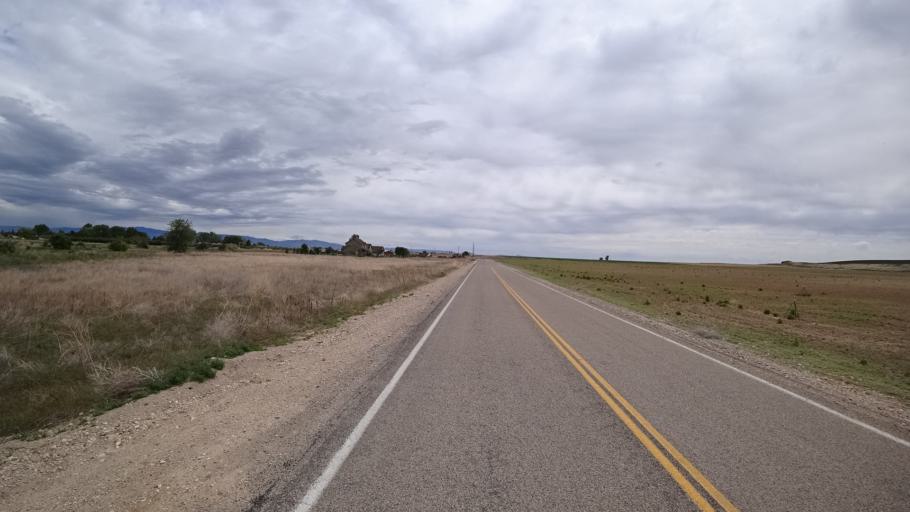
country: US
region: Idaho
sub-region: Ada County
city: Kuna
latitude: 43.4701
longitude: -116.4415
